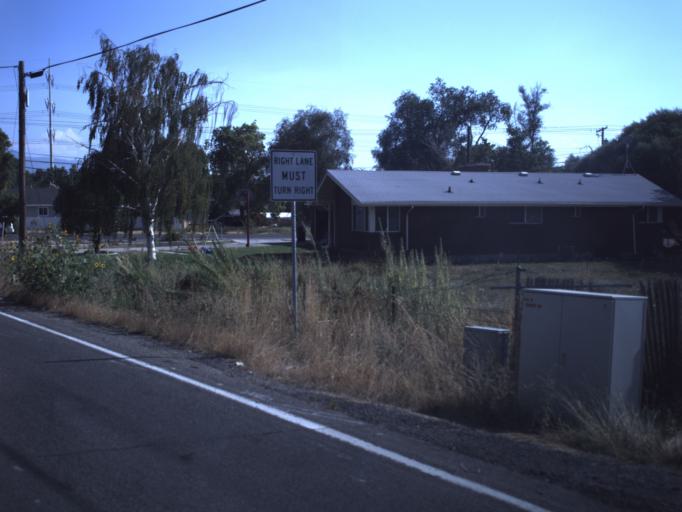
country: US
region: Utah
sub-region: Utah County
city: Provo
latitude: 40.2434
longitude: -111.6960
